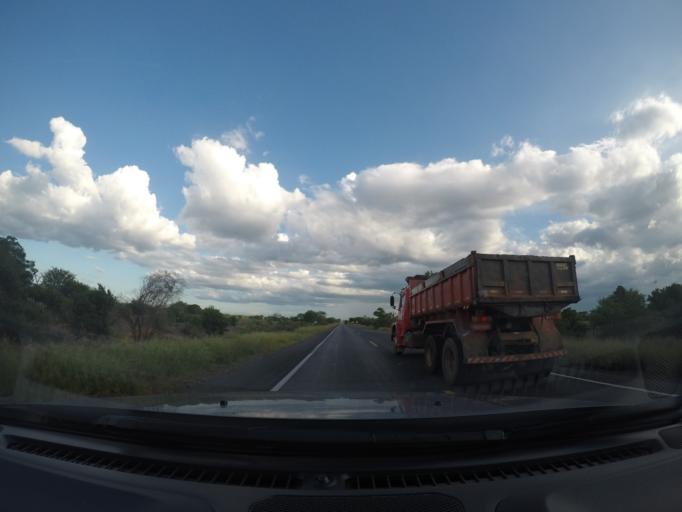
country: BR
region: Bahia
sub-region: Oliveira Dos Brejinhos
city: Beira Rio
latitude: -12.2404
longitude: -42.7718
